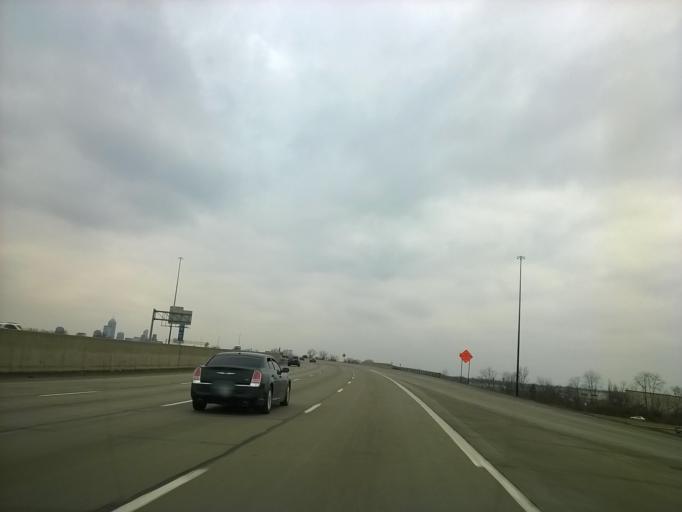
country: US
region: Indiana
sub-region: Marion County
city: Indianapolis
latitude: 39.7982
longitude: -86.1152
